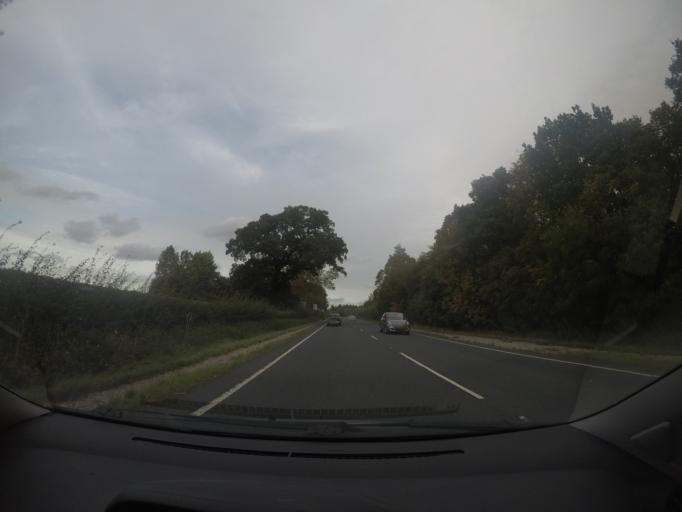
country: GB
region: England
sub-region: North Yorkshire
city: Riccall
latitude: 53.8482
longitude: -1.0520
